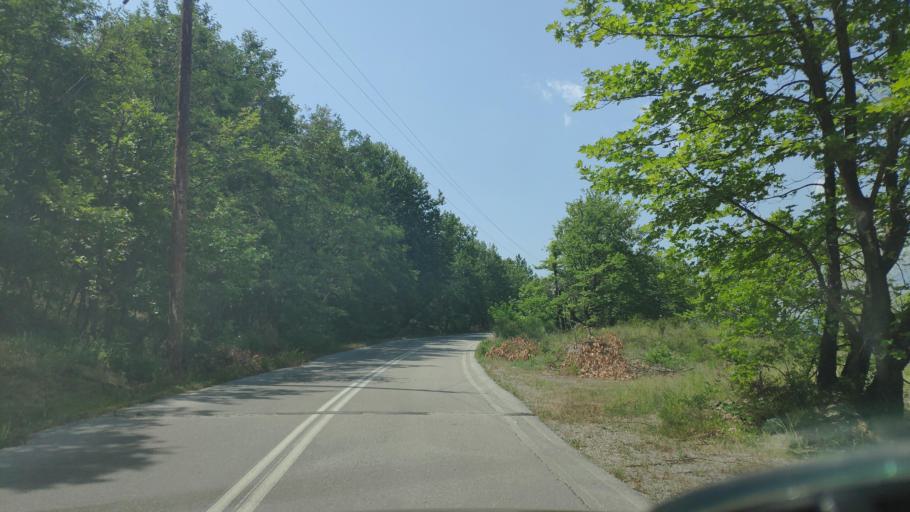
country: GR
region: Epirus
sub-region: Nomos Artas
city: Ano Kalentini
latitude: 39.2392
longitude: 21.1993
